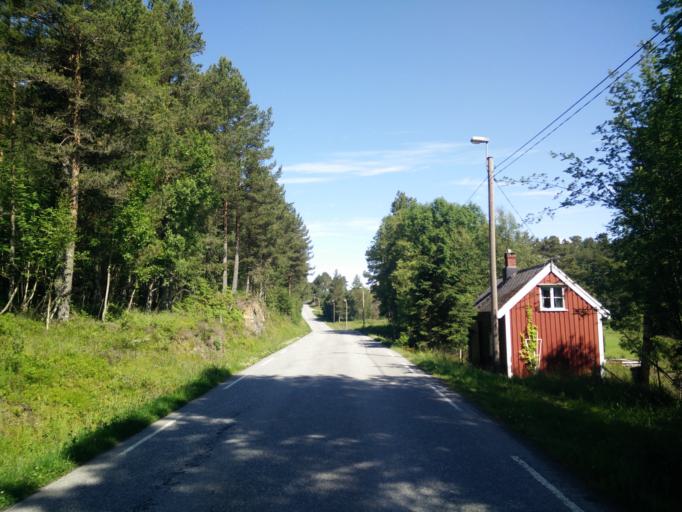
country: NO
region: More og Romsdal
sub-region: Kristiansund
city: Rensvik
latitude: 63.0593
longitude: 7.8685
